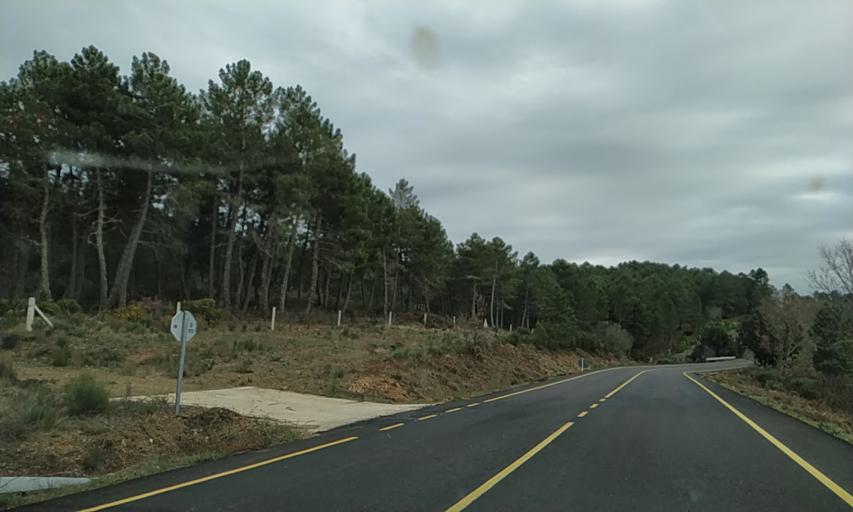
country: ES
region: Extremadura
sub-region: Provincia de Caceres
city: Acebo
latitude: 40.2535
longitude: -6.6882
